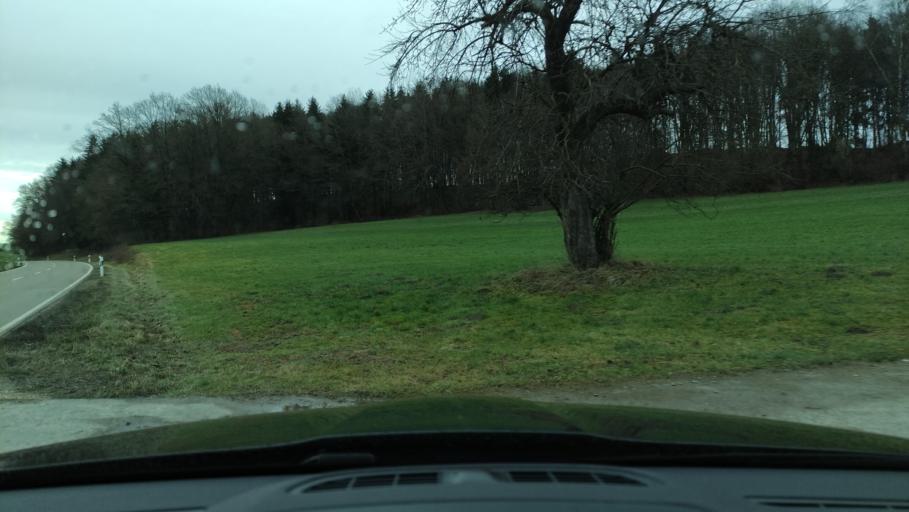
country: DE
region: Bavaria
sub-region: Swabia
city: Buch
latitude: 48.2392
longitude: 10.2033
